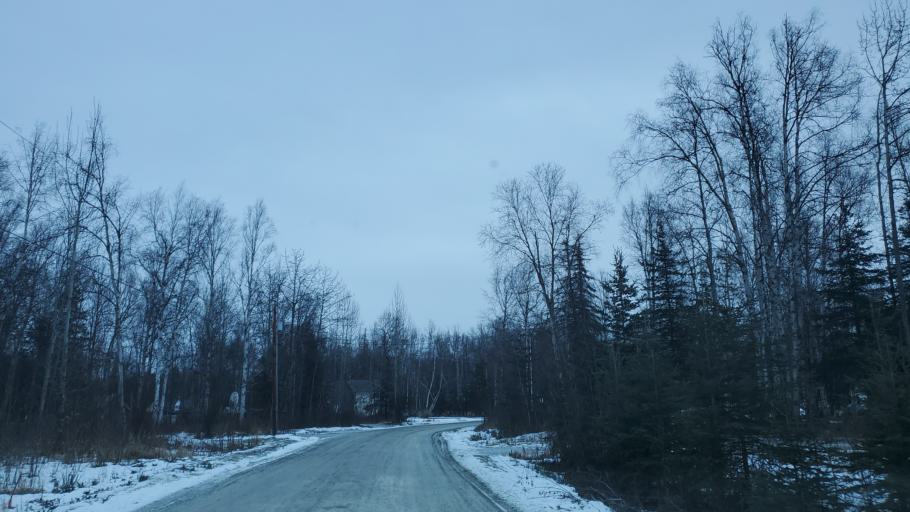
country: US
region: Alaska
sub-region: Matanuska-Susitna Borough
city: Lakes
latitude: 61.6674
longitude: -149.3011
